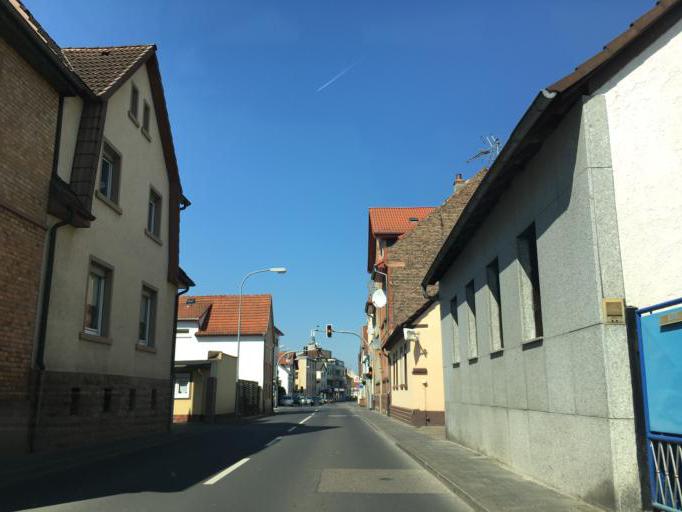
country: DE
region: Hesse
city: Obertshausen
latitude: 50.0953
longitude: 8.8581
